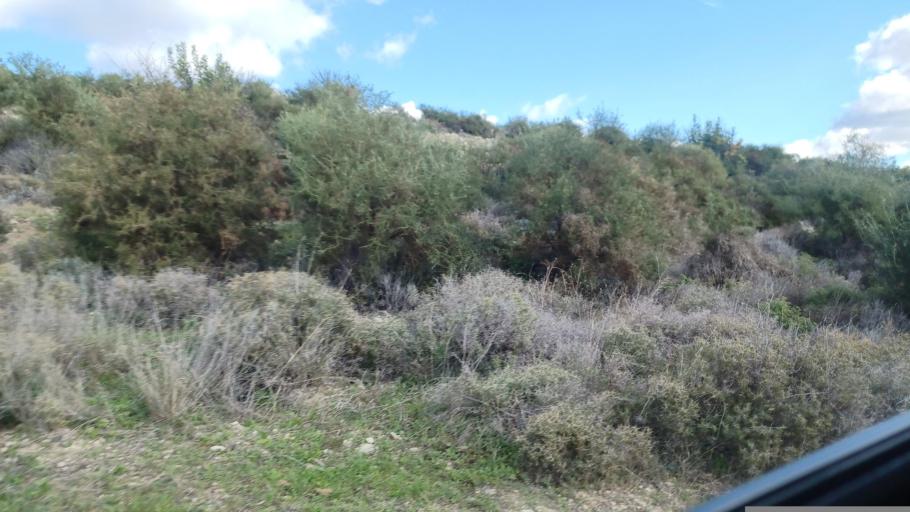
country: CY
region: Limassol
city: Pano Polemidia
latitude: 34.7693
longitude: 32.9798
